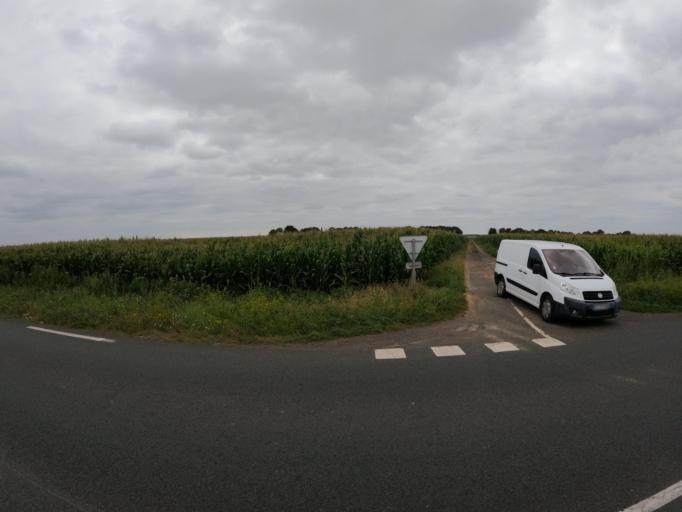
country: FR
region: Pays de la Loire
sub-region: Departement de la Vendee
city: Sainte-Hermine
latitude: 46.5425
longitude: -1.0281
